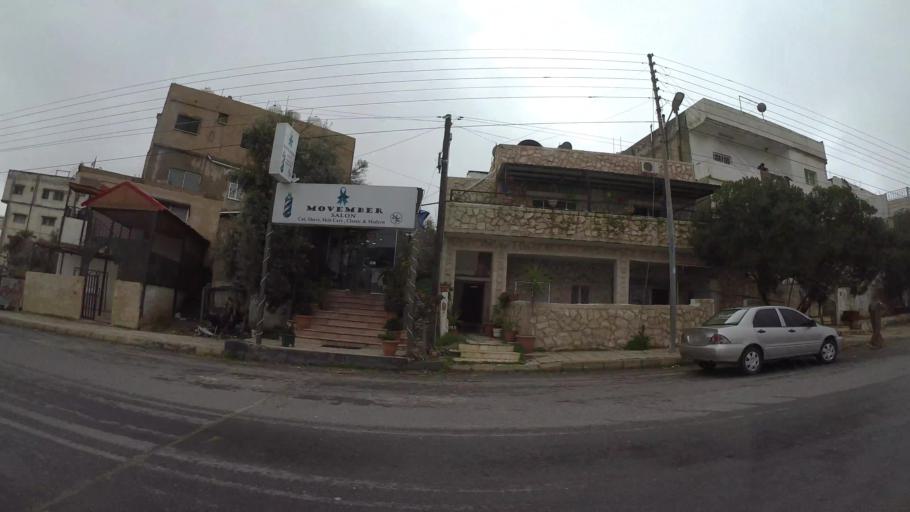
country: JO
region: Amman
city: Al Bunayyat ash Shamaliyah
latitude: 31.9431
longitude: 35.8874
